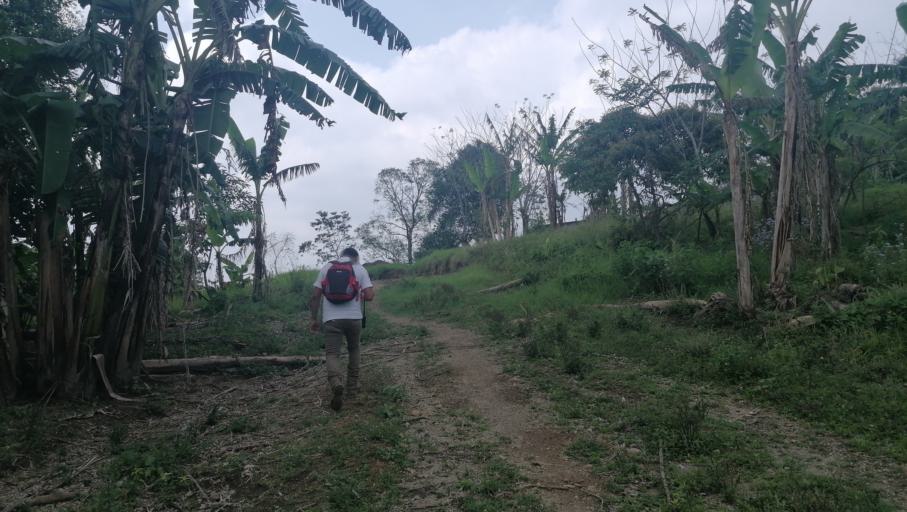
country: MX
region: Chiapas
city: Ostuacan
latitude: 17.3607
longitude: -93.3180
